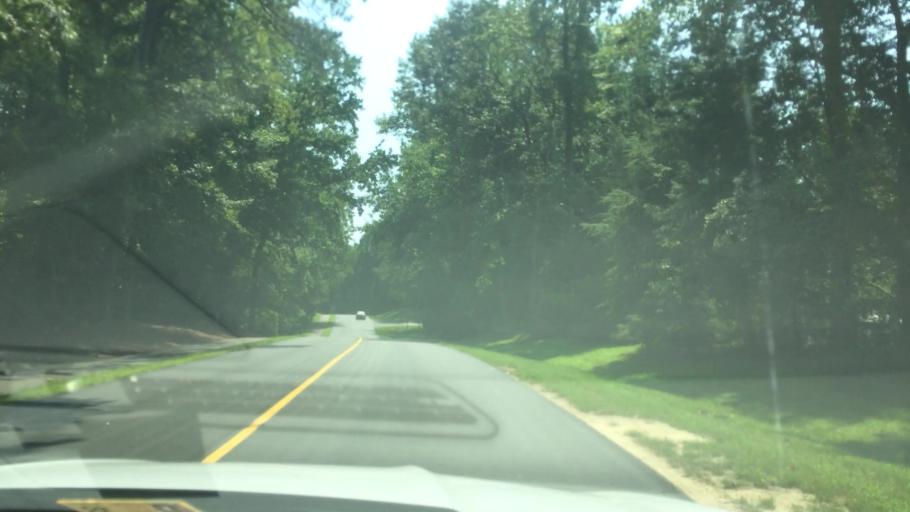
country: US
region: Virginia
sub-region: James City County
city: Williamsburg
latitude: 37.2972
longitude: -76.7686
